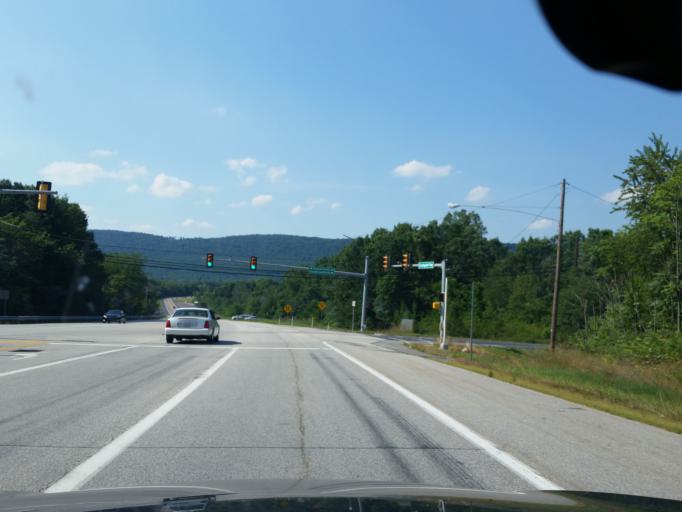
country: US
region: Pennsylvania
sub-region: Cumberland County
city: Mechanicsburg
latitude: 40.2729
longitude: -77.0454
